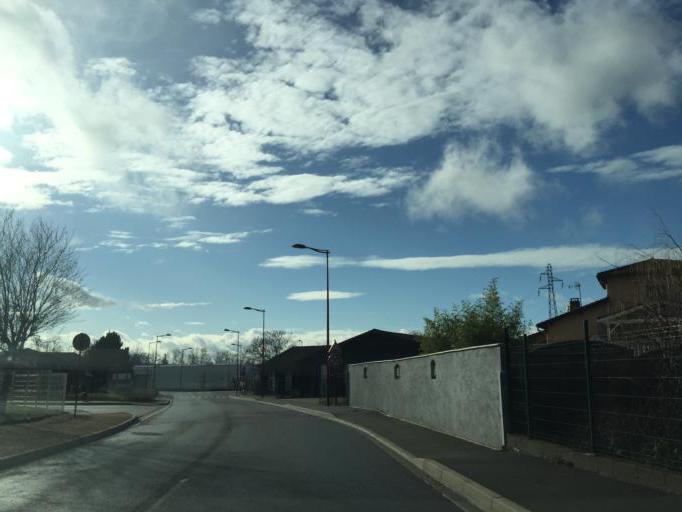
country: FR
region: Rhone-Alpes
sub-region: Departement de la Loire
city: Sorbiers
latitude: 45.4790
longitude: 4.4500
